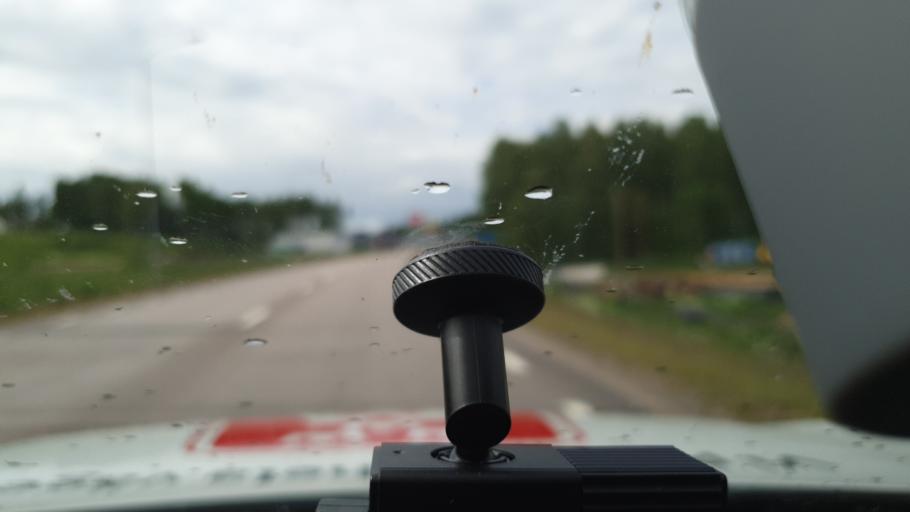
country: SE
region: Vaermland
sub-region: Torsby Kommun
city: Torsby
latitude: 60.1338
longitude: 12.9904
